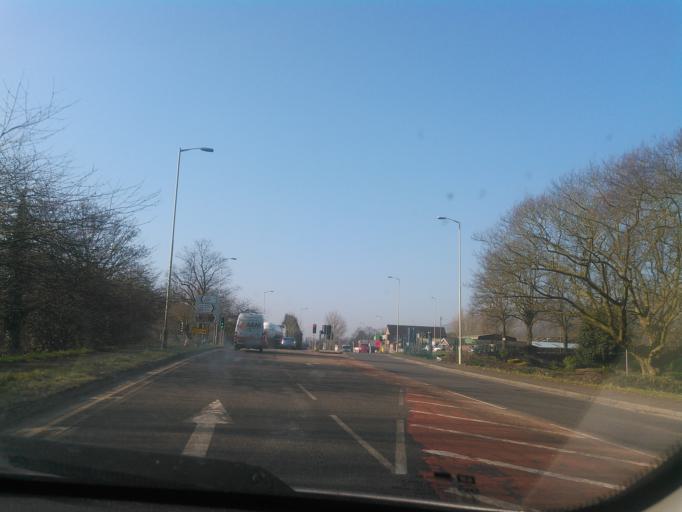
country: GB
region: England
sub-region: Shropshire
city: Church Stretton
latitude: 52.5383
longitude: -2.8005
